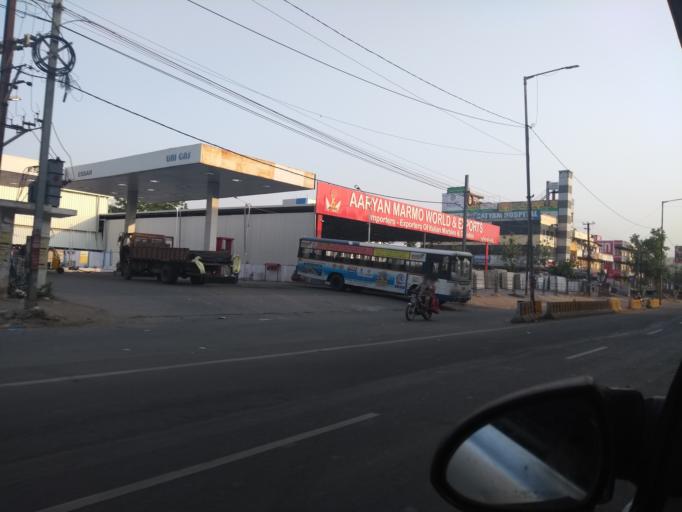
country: IN
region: Telangana
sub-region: Hyderabad
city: Hyderabad
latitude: 17.3660
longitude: 78.4285
